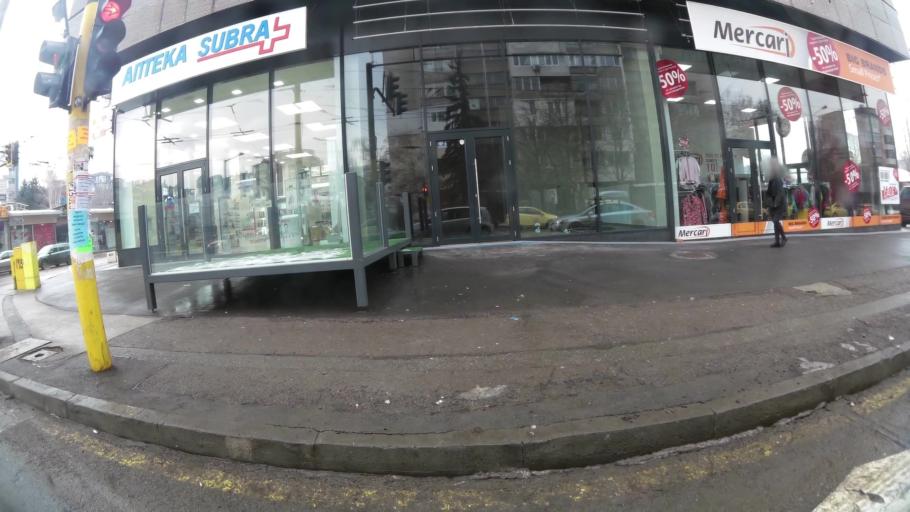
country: BG
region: Sofia-Capital
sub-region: Stolichna Obshtina
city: Sofia
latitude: 42.6685
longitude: 23.2794
